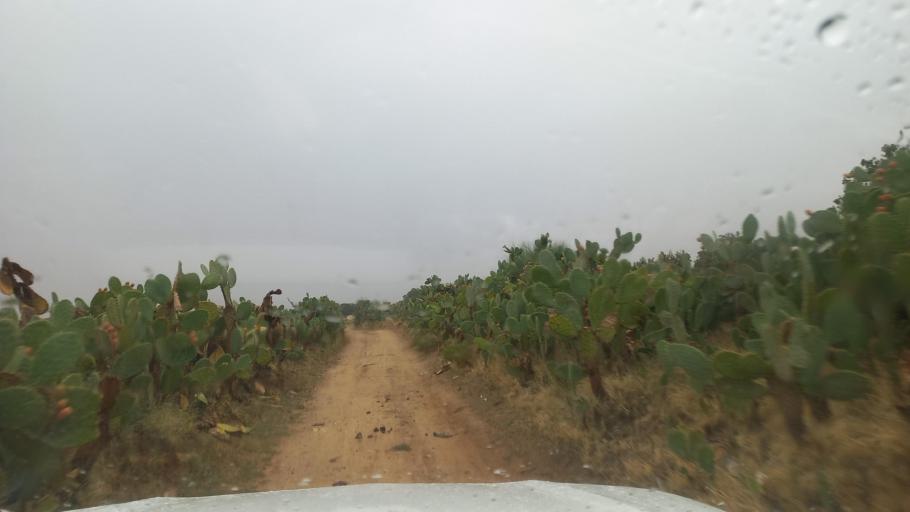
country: TN
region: Al Qasrayn
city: Kasserine
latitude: 35.2709
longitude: 8.9452
